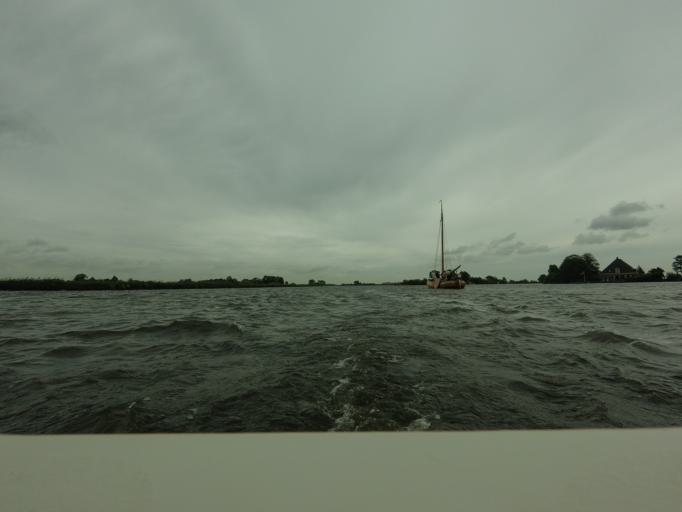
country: NL
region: Friesland
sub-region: Gemeente Boarnsterhim
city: Grou
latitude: 53.1041
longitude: 5.8535
